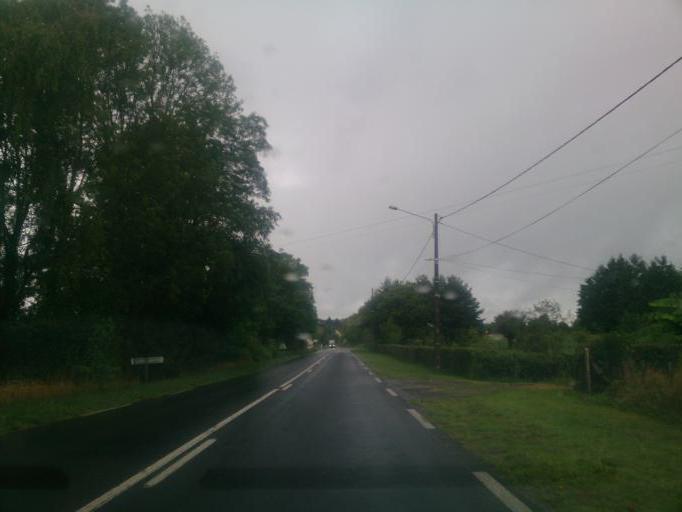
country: FR
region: Limousin
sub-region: Departement de la Correze
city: Sainte-Fereole
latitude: 45.2000
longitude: 1.5787
